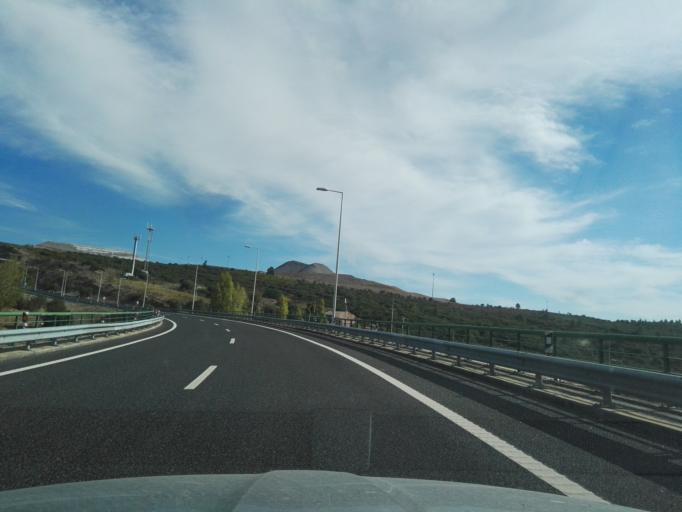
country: PT
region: Lisbon
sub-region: Vila Franca de Xira
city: Vialonga
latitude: 38.9089
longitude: -9.0731
